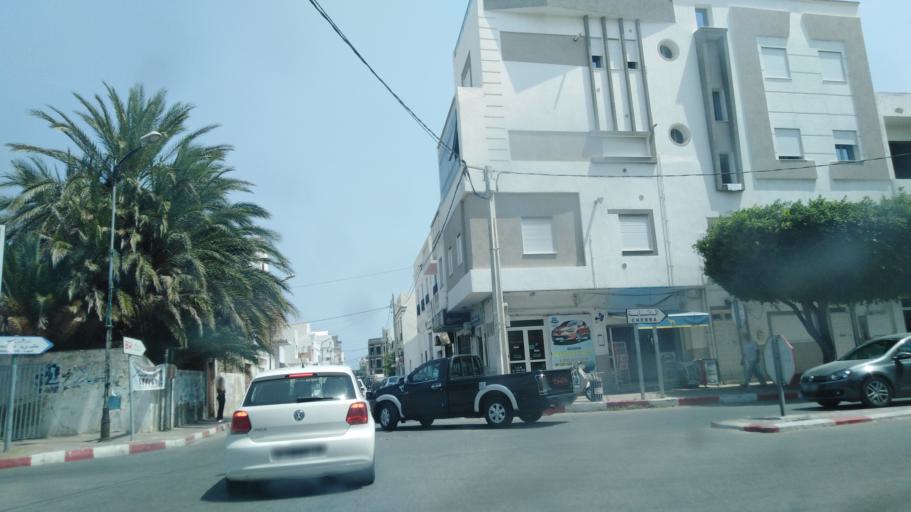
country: TN
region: Al Mahdiyah
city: Mahdia
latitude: 35.5076
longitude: 11.0565
